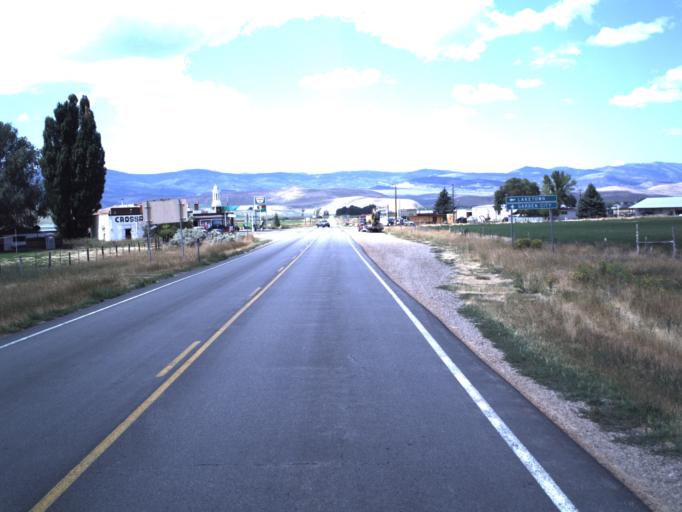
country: US
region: Utah
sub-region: Rich County
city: Randolph
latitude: 41.8309
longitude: -111.3208
